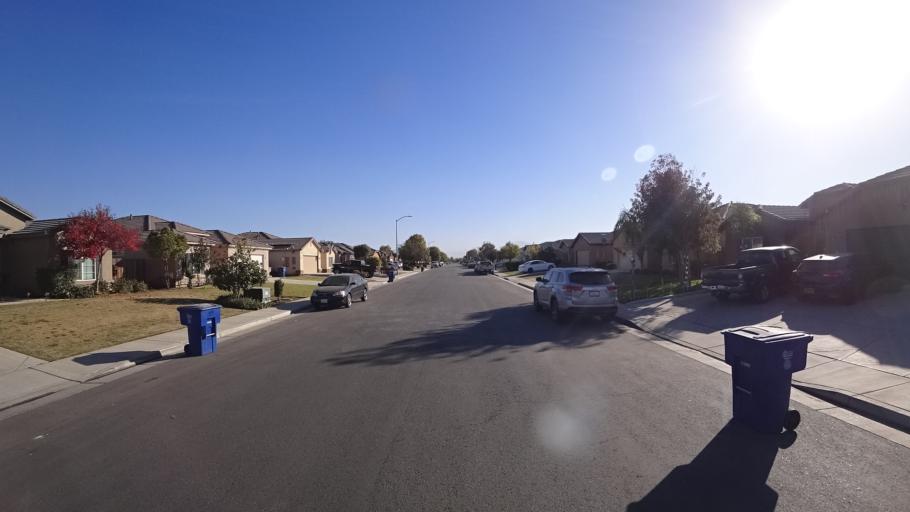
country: US
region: California
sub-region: Kern County
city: Greenfield
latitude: 35.2692
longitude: -119.0448
